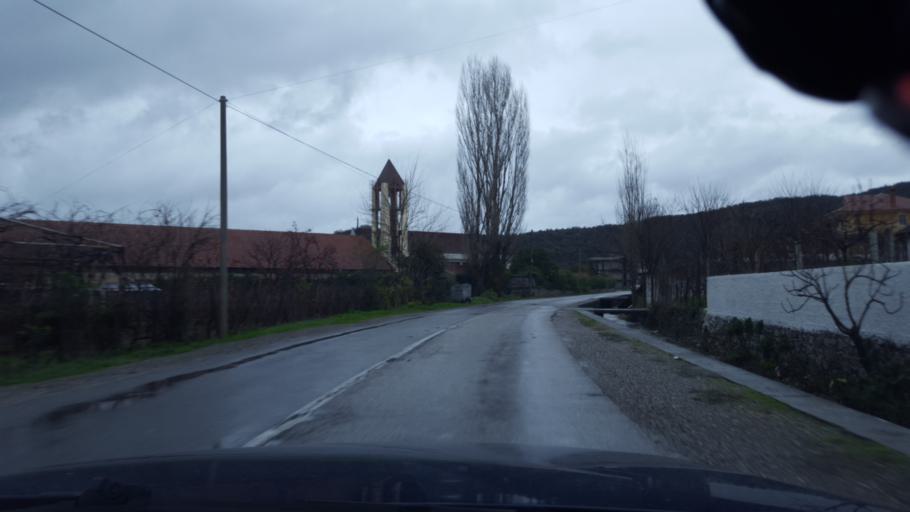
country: AL
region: Shkoder
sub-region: Rrethi i Shkodres
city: Berdica e Madhe
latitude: 42.0153
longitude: 19.4823
